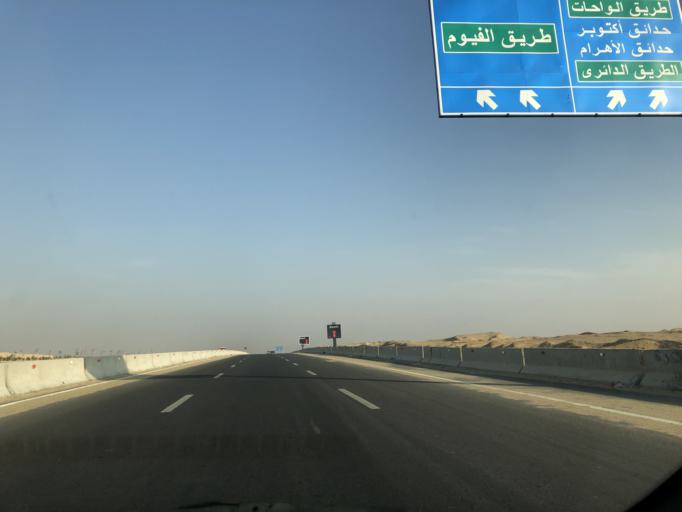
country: EG
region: Al Jizah
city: Madinat Sittah Uktubar
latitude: 29.8987
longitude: 30.9926
